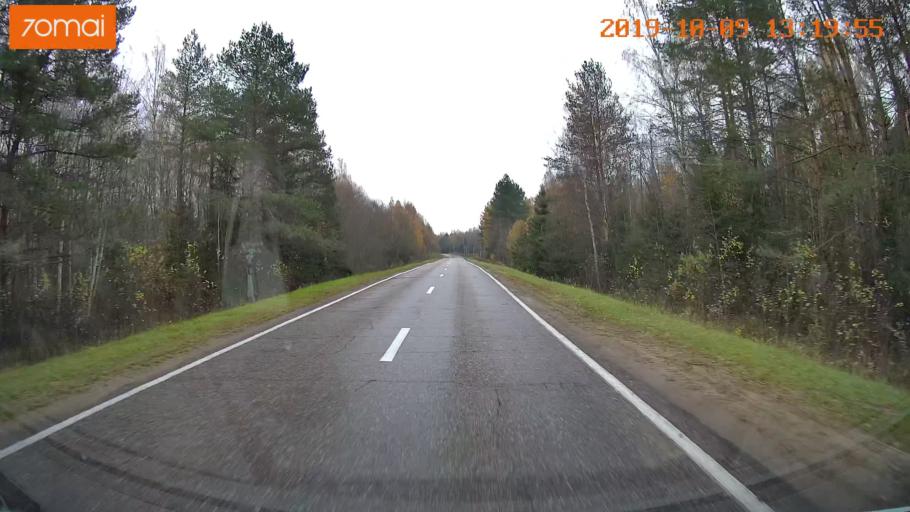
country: RU
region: Jaroslavl
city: Lyubim
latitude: 58.3466
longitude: 40.8224
